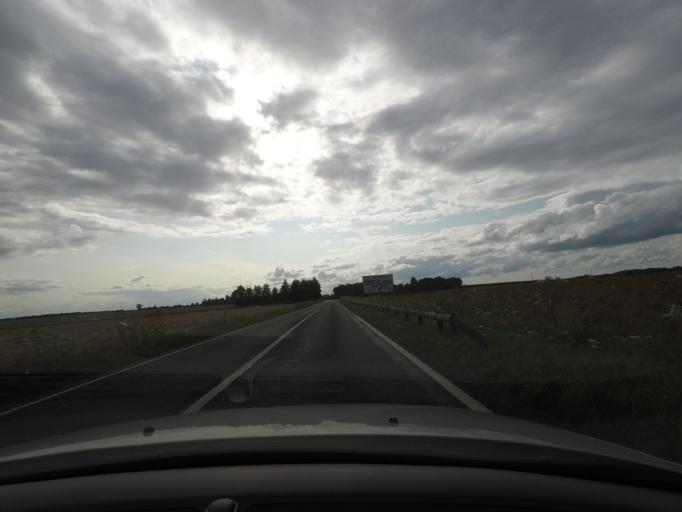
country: FR
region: Haute-Normandie
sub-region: Departement de la Seine-Maritime
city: Les Authieux-sur-le-Port-Saint-Ouen
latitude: 49.3448
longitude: 1.1517
